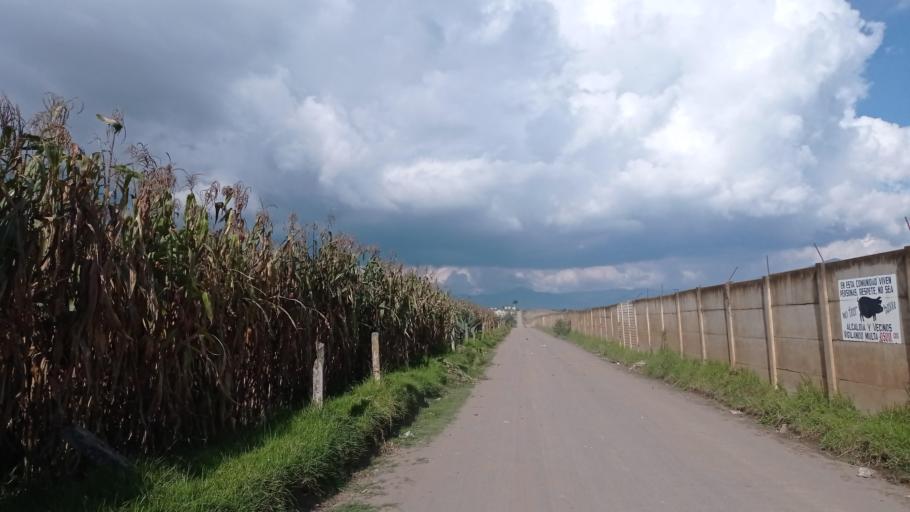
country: GT
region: Quetzaltenango
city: Olintepeque
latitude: 14.8643
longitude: -91.5062
